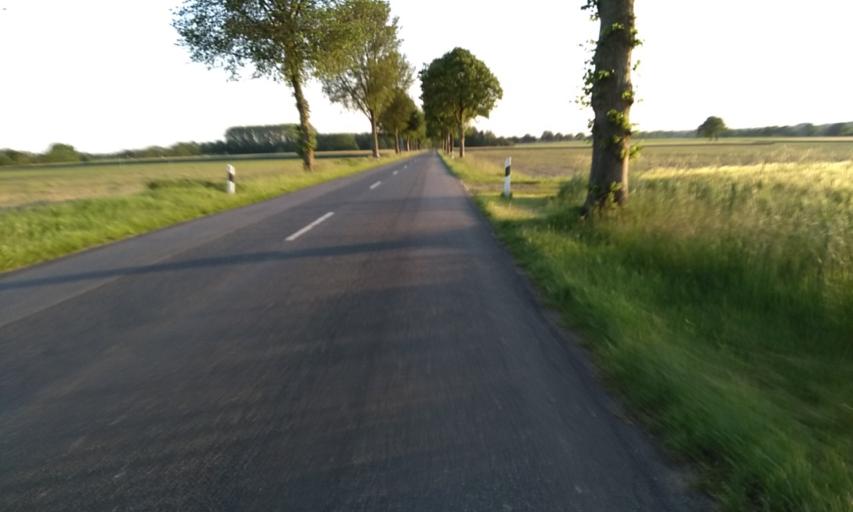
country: DE
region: Lower Saxony
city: Ahlerstedt
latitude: 53.4312
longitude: 9.4574
